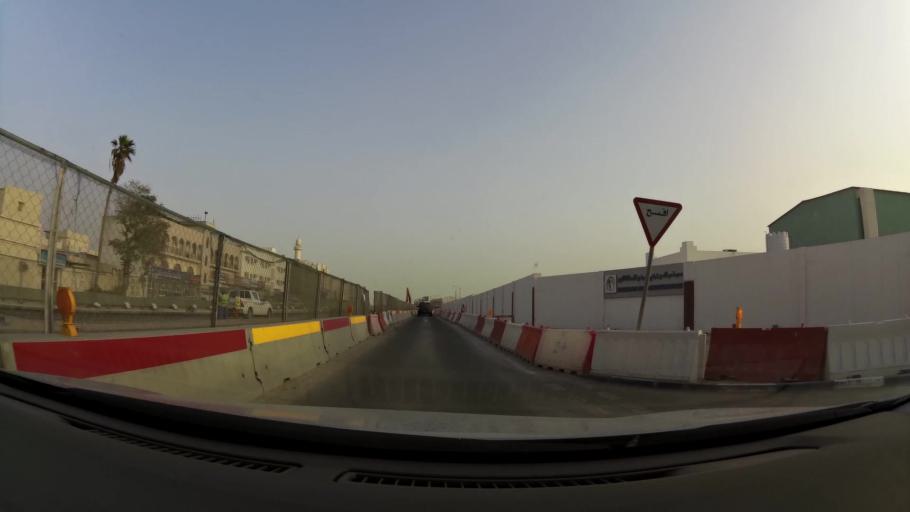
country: QA
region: Baladiyat ar Rayyan
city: Ar Rayyan
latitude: 25.2468
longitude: 51.4530
